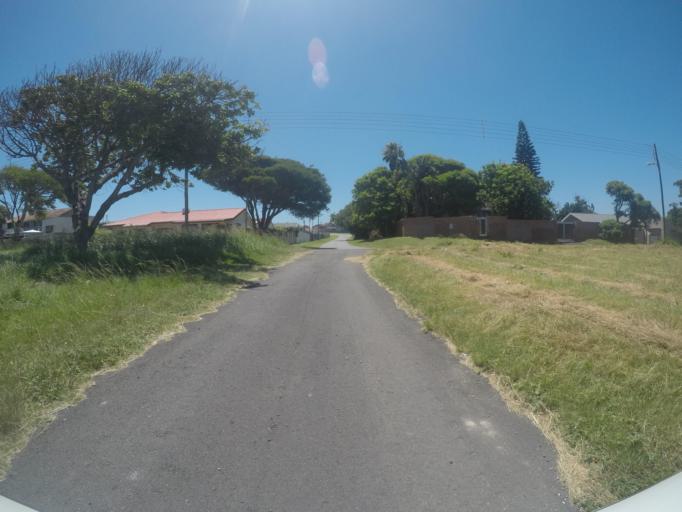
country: ZA
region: Eastern Cape
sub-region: Buffalo City Metropolitan Municipality
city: East London
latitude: -32.9571
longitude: 27.9966
